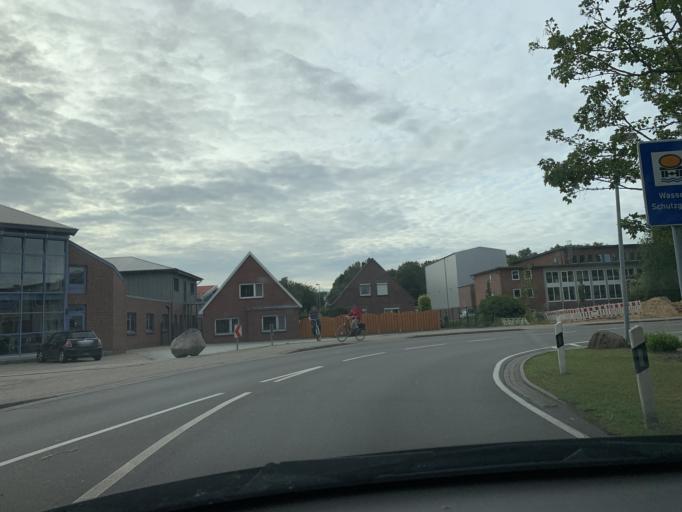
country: DE
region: Lower Saxony
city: Westerstede
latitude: 53.2660
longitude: 7.9361
